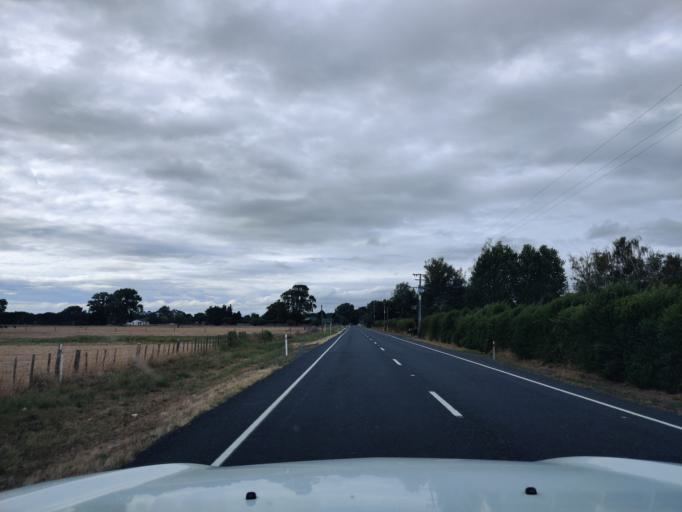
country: NZ
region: Waikato
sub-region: Waipa District
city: Cambridge
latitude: -37.8342
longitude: 175.4537
